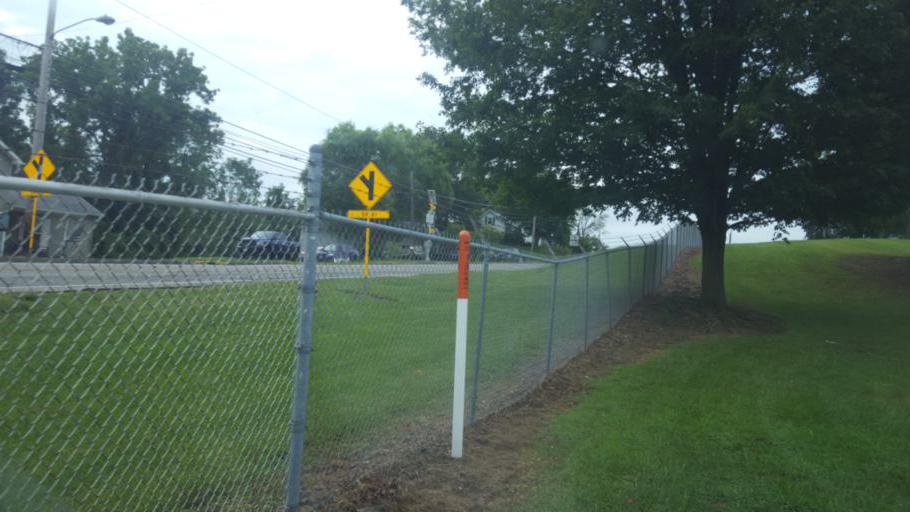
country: US
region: Ohio
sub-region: Morrow County
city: Mount Gilead
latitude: 40.5418
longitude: -82.8305
